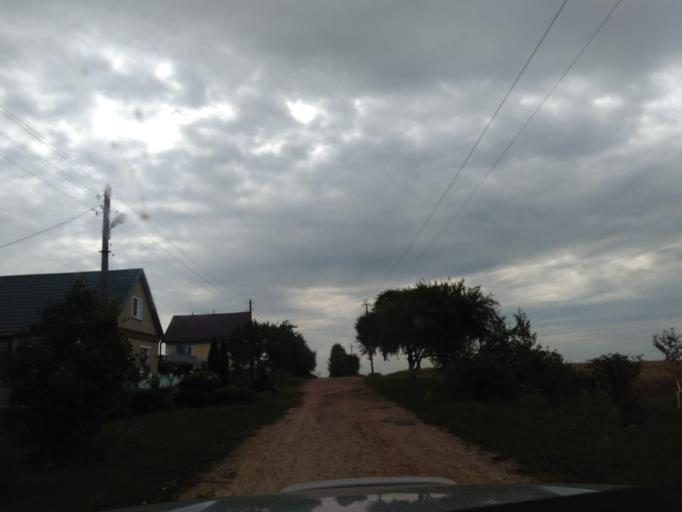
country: BY
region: Minsk
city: Kapyl'
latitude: 53.1527
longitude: 27.0706
